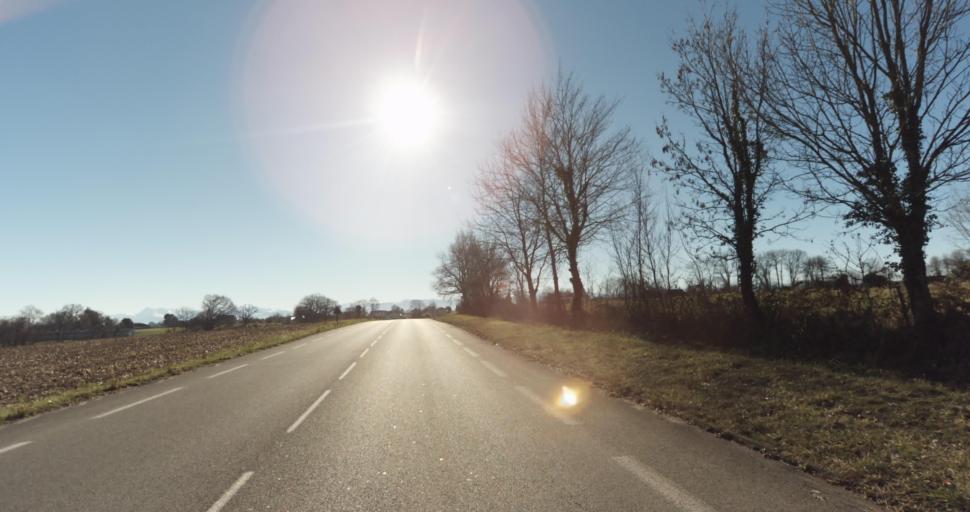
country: FR
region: Aquitaine
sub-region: Departement des Pyrenees-Atlantiques
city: Morlaas
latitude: 43.3428
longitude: -0.2759
